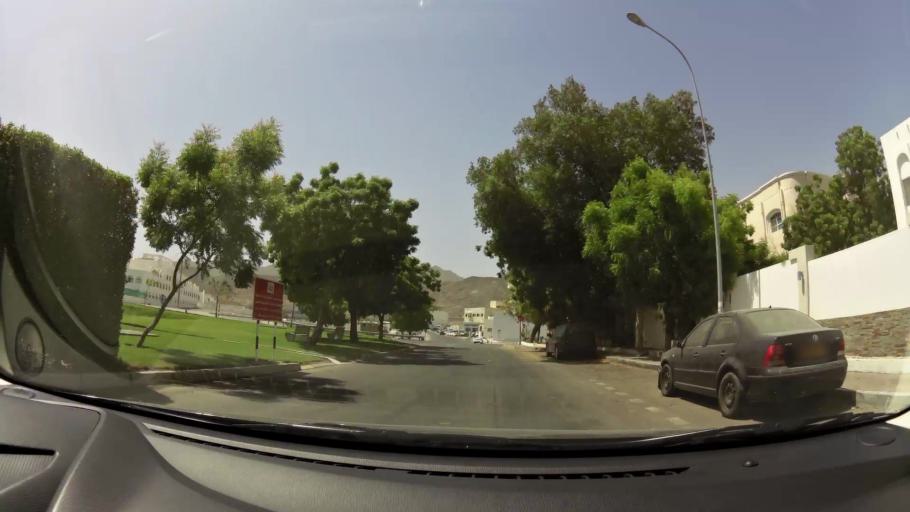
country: OM
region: Muhafazat Masqat
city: Bawshar
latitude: 23.5945
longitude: 58.4569
